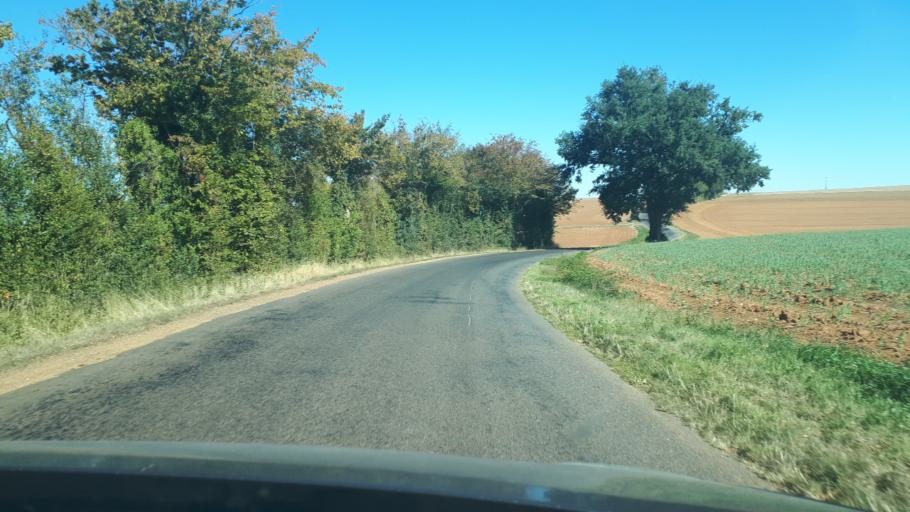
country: FR
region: Centre
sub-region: Departement du Cher
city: Sancerre
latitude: 47.3206
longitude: 2.7710
